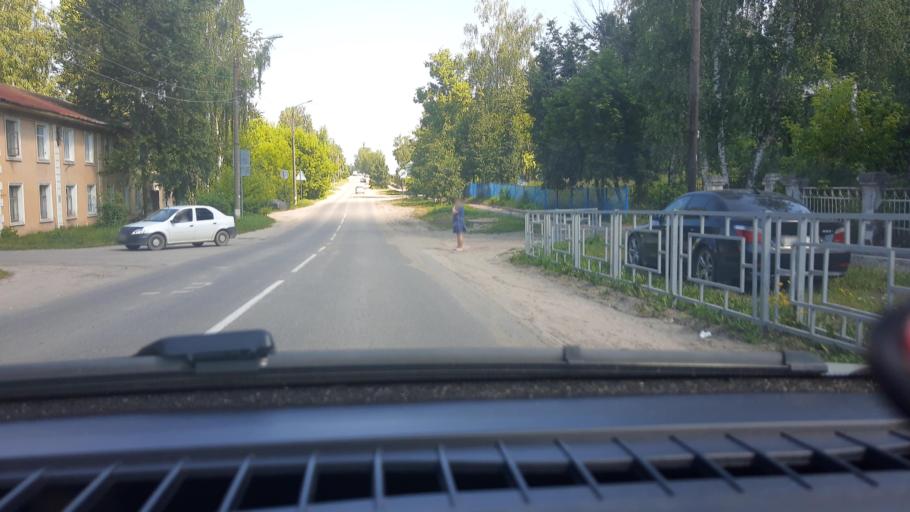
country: RU
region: Nizjnij Novgorod
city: Afonino
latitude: 56.2859
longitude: 44.1909
